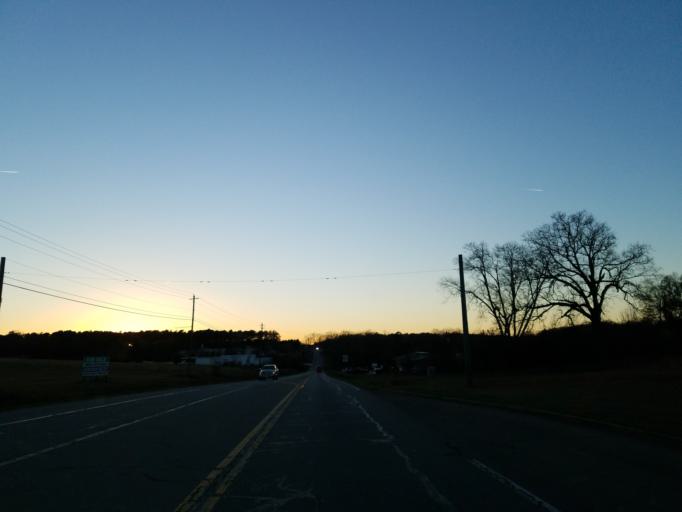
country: US
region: Georgia
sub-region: Monroe County
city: Forsyth
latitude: 33.0276
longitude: -83.9139
